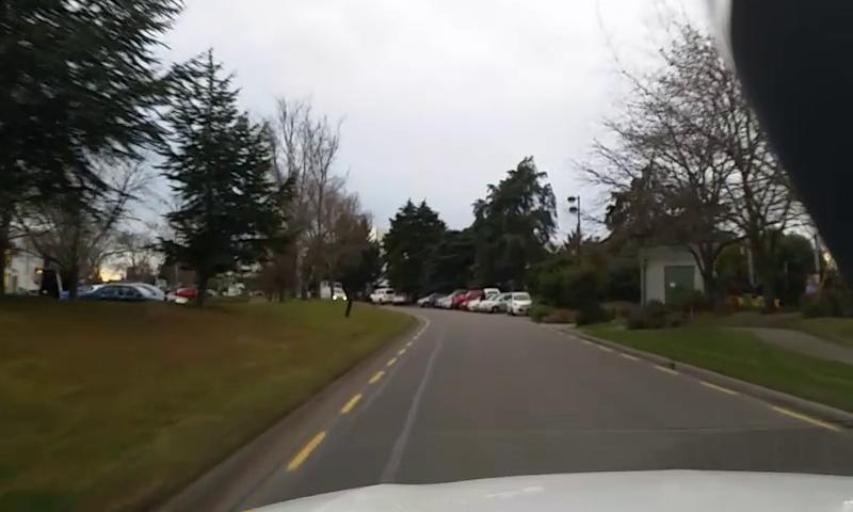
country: NZ
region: Canterbury
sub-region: Christchurch City
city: Christchurch
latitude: -43.4939
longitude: 172.5598
